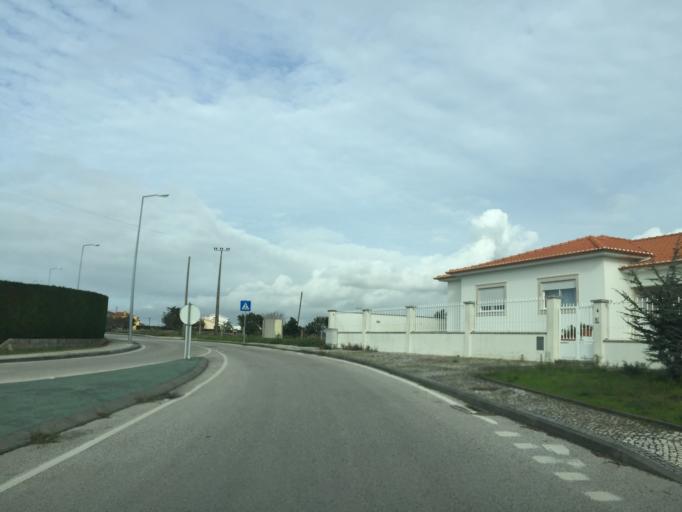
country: PT
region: Coimbra
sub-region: Figueira da Foz
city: Lavos
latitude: 40.0681
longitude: -8.8022
